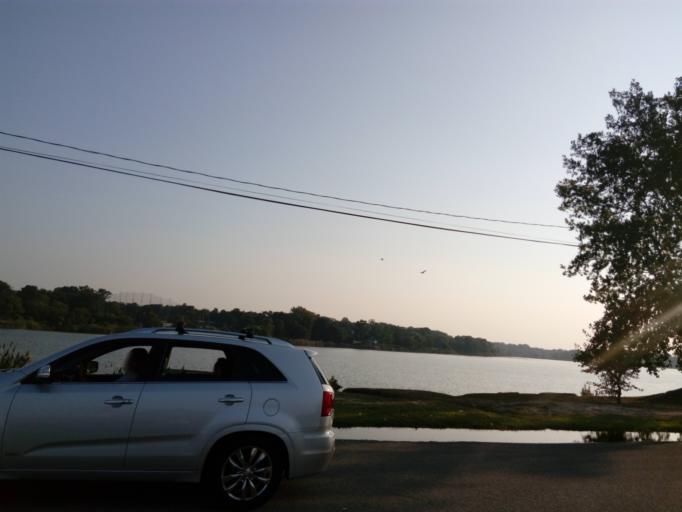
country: US
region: New York
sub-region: Nassau County
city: Lattingtown
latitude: 40.8981
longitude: -73.6230
